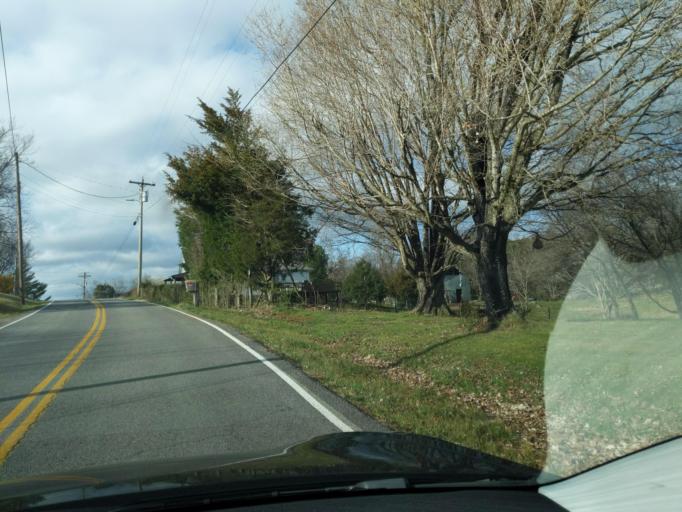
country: US
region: Tennessee
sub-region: Jefferson County
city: Dandridge
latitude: 36.0234
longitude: -83.4126
